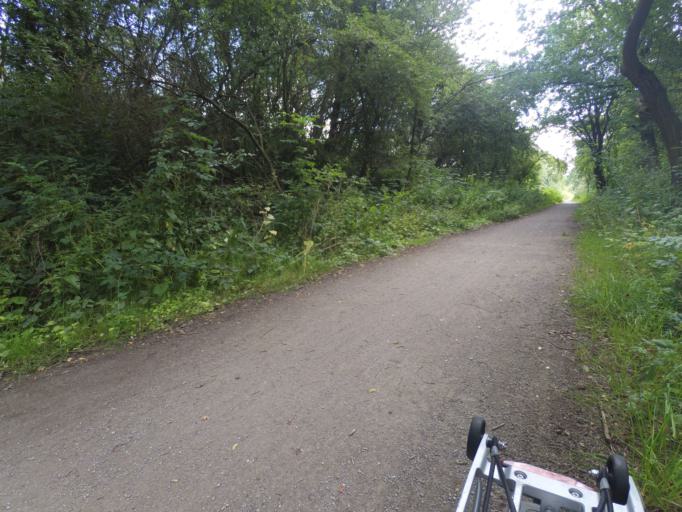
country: GB
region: England
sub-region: Shropshire
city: Woodcote
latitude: 52.7625
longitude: -2.3374
